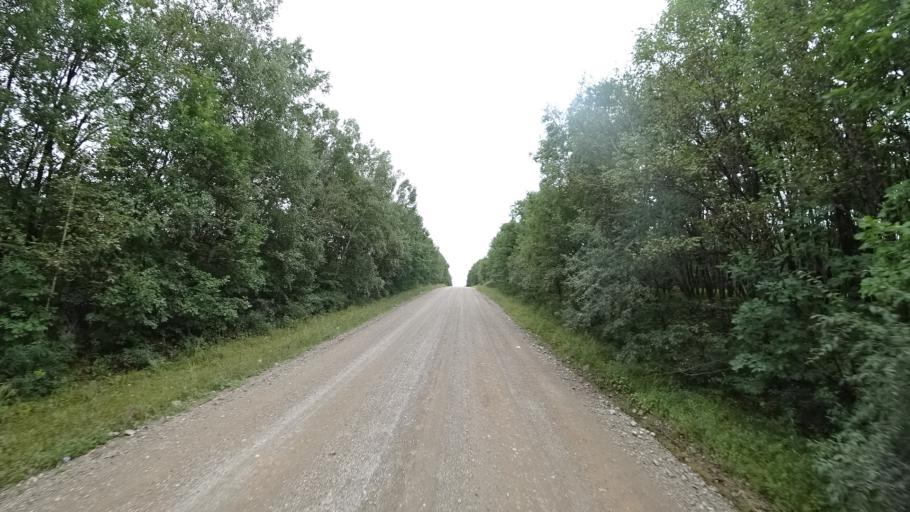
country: RU
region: Primorskiy
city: Ivanovka
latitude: 44.0244
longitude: 132.5172
